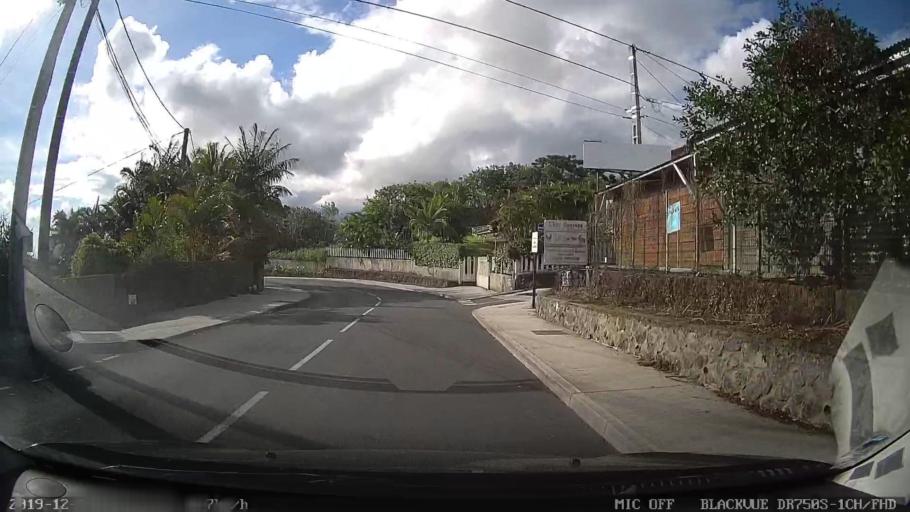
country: RE
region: Reunion
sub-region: Reunion
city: Le Tampon
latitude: -21.2463
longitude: 55.5170
